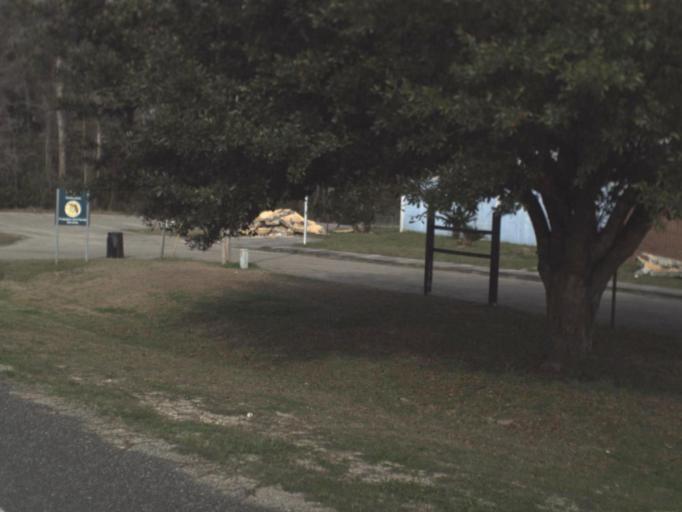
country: US
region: Florida
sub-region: Jefferson County
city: Monticello
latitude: 30.5301
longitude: -83.8710
